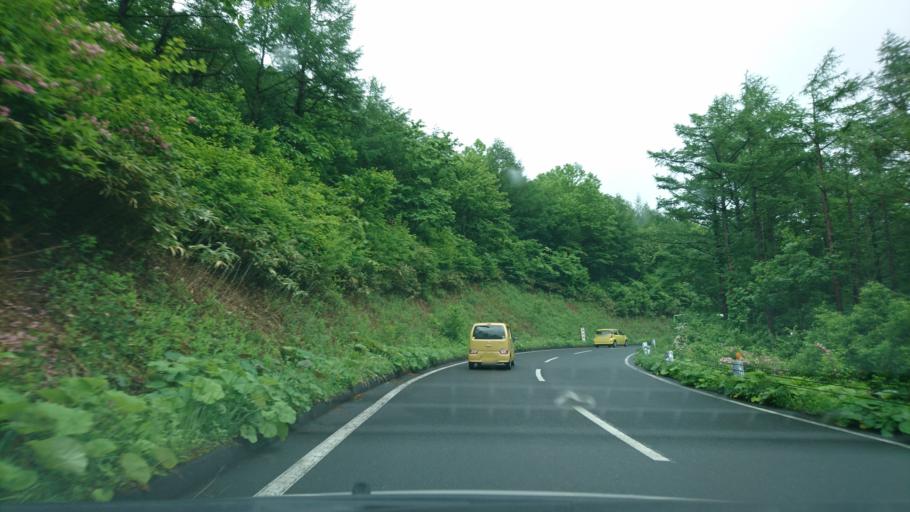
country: JP
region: Iwate
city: Ichinoseki
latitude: 38.9963
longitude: 140.8255
